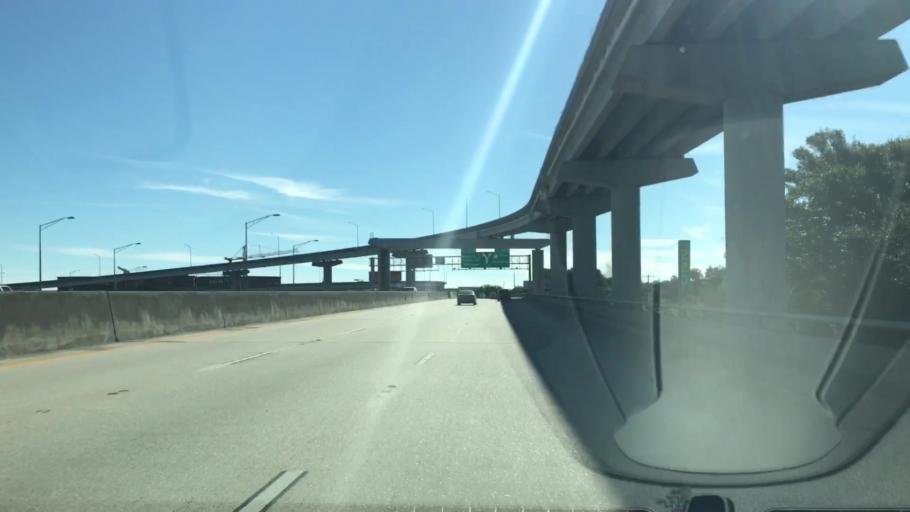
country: US
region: South Carolina
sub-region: Charleston County
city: Charleston
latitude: 32.8059
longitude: -79.9487
